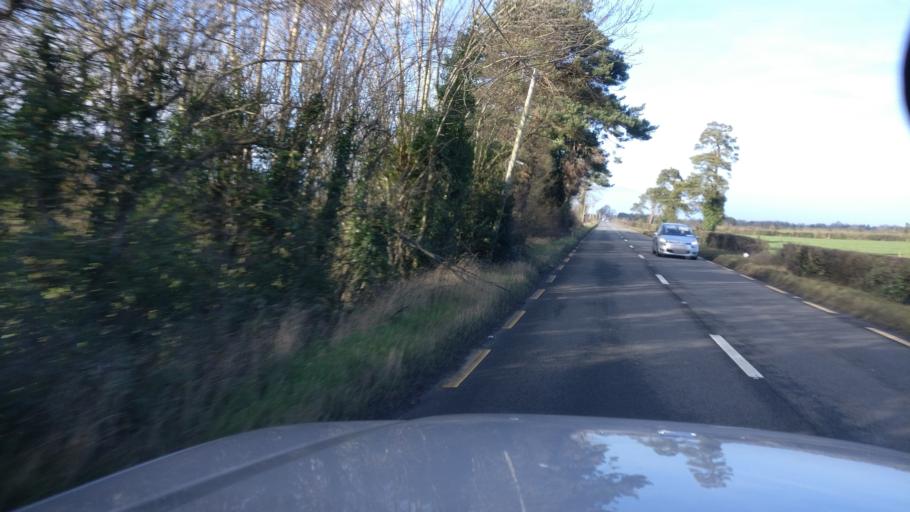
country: IE
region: Leinster
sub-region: Laois
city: Mountmellick
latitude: 53.0886
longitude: -7.3344
